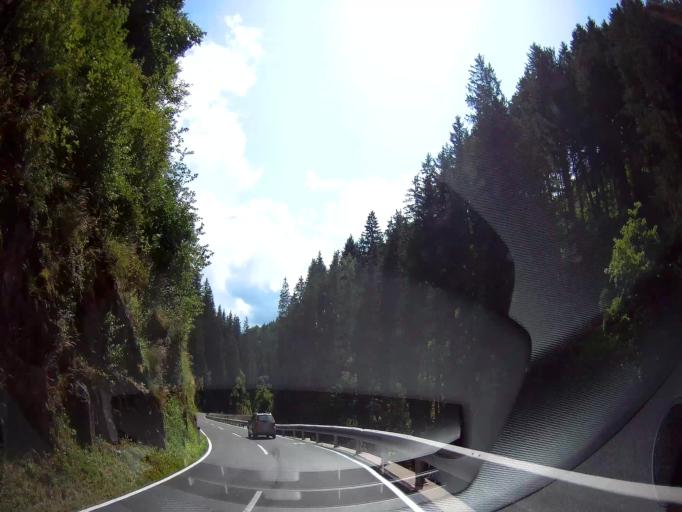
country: AT
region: Carinthia
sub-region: Politischer Bezirk Spittal an der Drau
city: Trebesing
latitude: 46.8542
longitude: 13.5010
